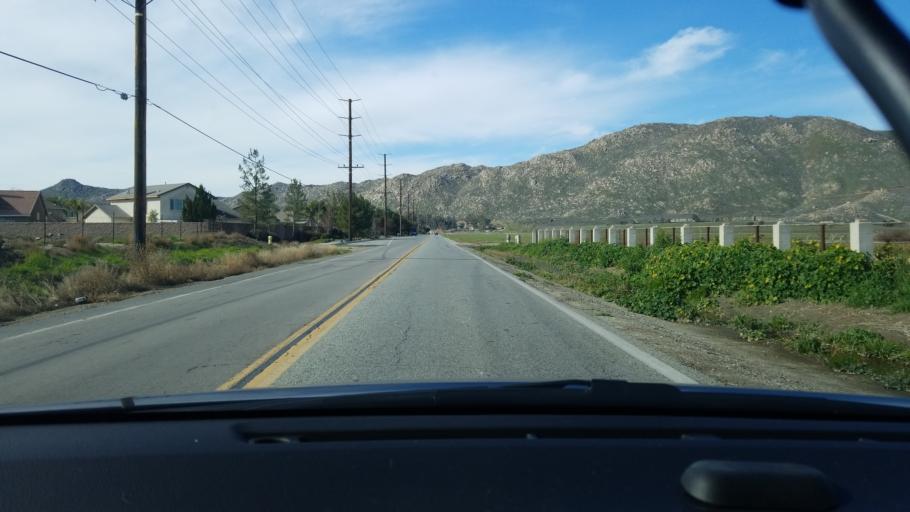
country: US
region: California
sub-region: Riverside County
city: Hemet
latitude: 33.7729
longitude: -117.0232
